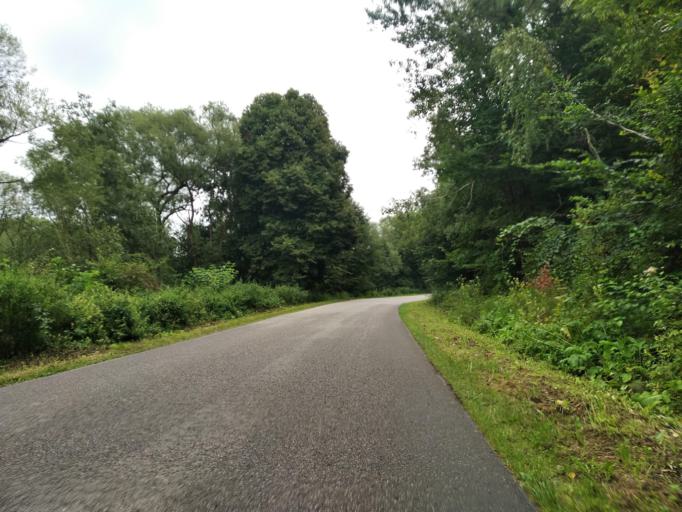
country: PL
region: Subcarpathian Voivodeship
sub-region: Powiat brzozowski
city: Nozdrzec
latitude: 49.7352
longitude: 22.2620
